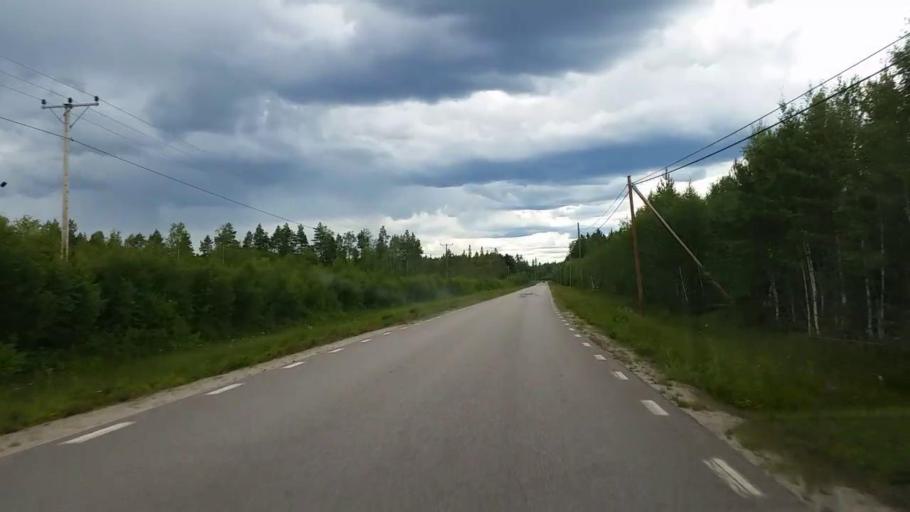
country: SE
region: Gaevleborg
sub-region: Ovanakers Kommun
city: Edsbyn
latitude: 61.4519
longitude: 15.8792
